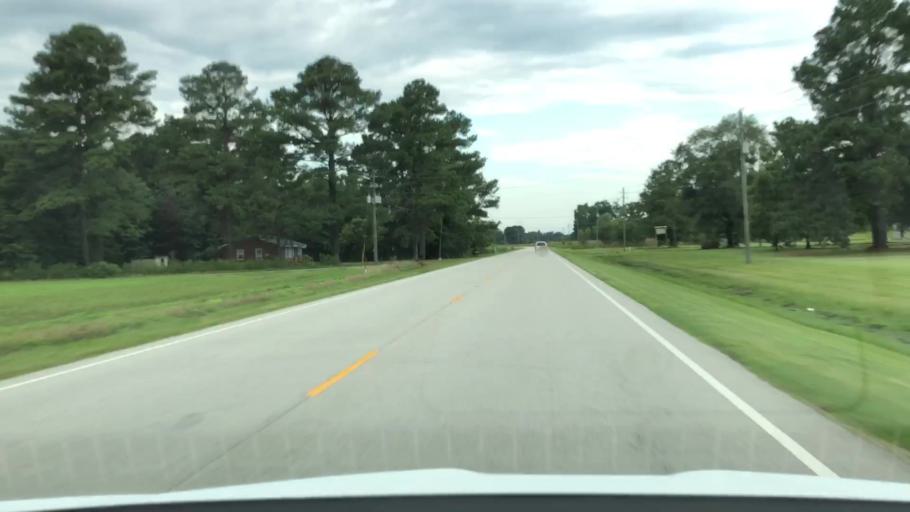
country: US
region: North Carolina
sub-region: Jones County
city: Trenton
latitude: 35.0764
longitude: -77.3924
